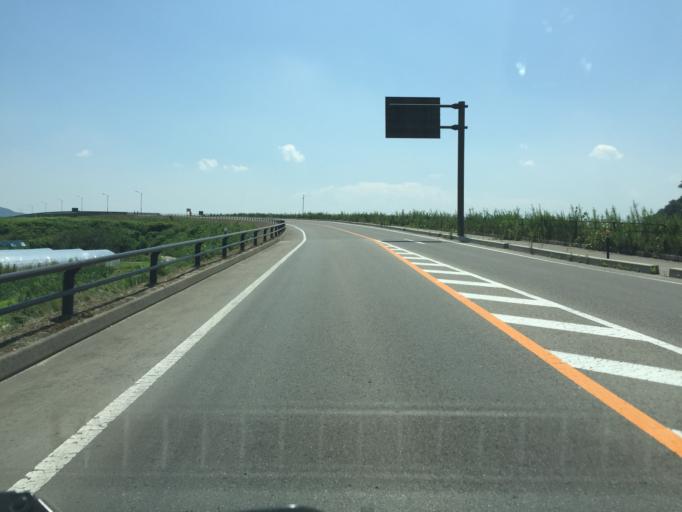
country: JP
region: Fukushima
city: Yanagawamachi-saiwaicho
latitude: 37.8731
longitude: 140.6090
